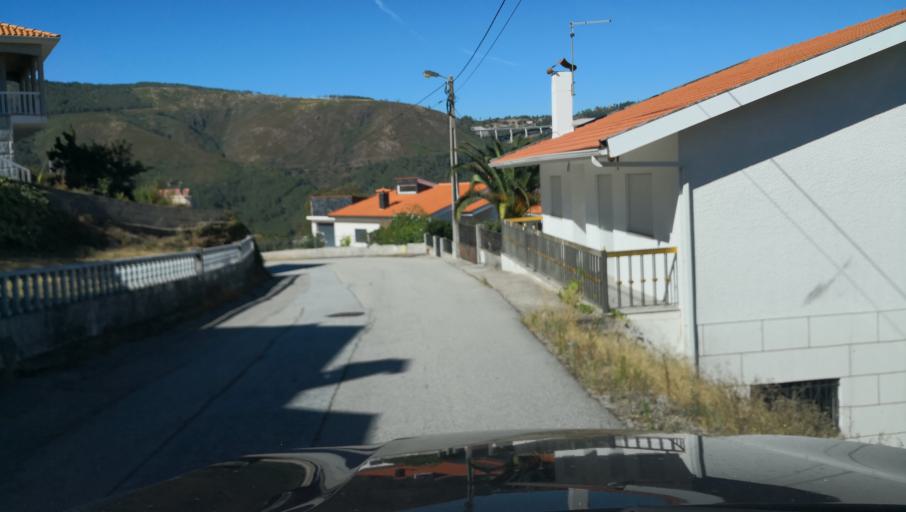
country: PT
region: Vila Real
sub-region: Santa Marta de Penaguiao
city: Santa Marta de Penaguiao
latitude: 41.2605
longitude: -7.8610
